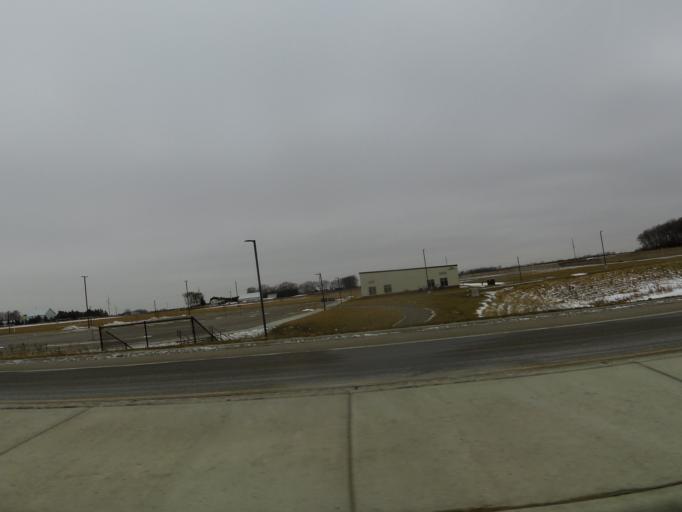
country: US
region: Minnesota
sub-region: Carver County
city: Waconia
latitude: 44.8352
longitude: -93.8240
